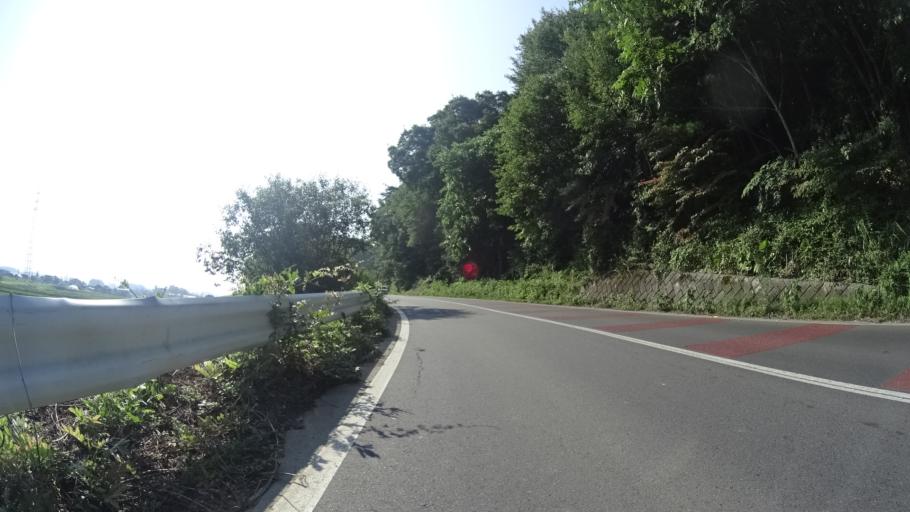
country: JP
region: Nagano
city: Chino
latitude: 35.9676
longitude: 138.1891
